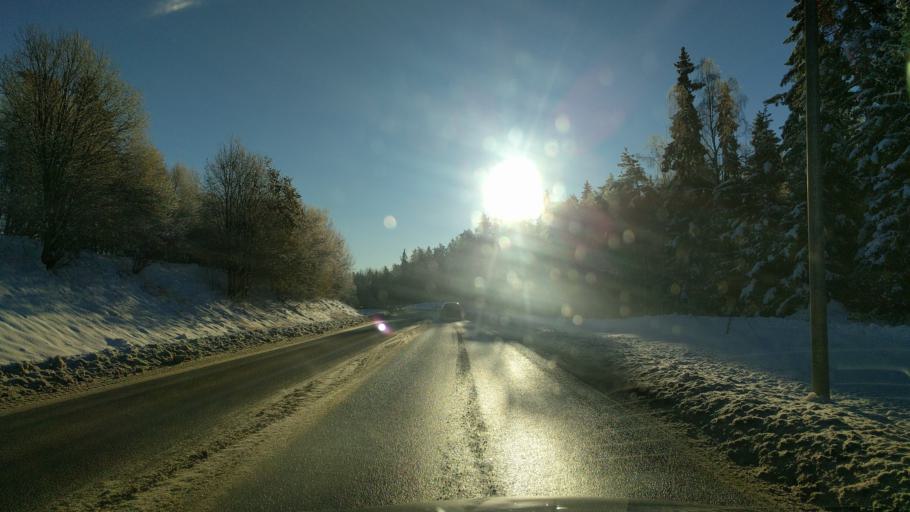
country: SE
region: Stockholm
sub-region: Taby Kommun
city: Taby
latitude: 59.4594
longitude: 18.0777
